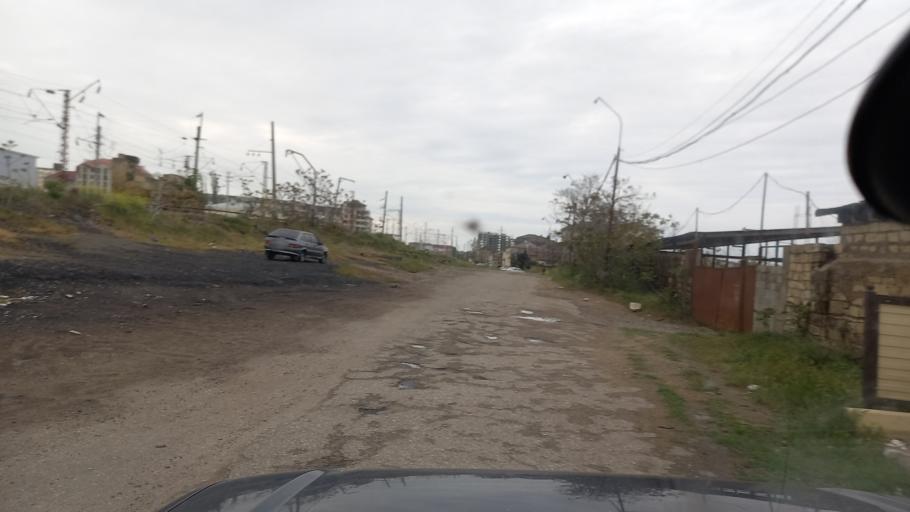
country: RU
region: Dagestan
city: Derbent
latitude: 42.0631
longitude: 48.3050
